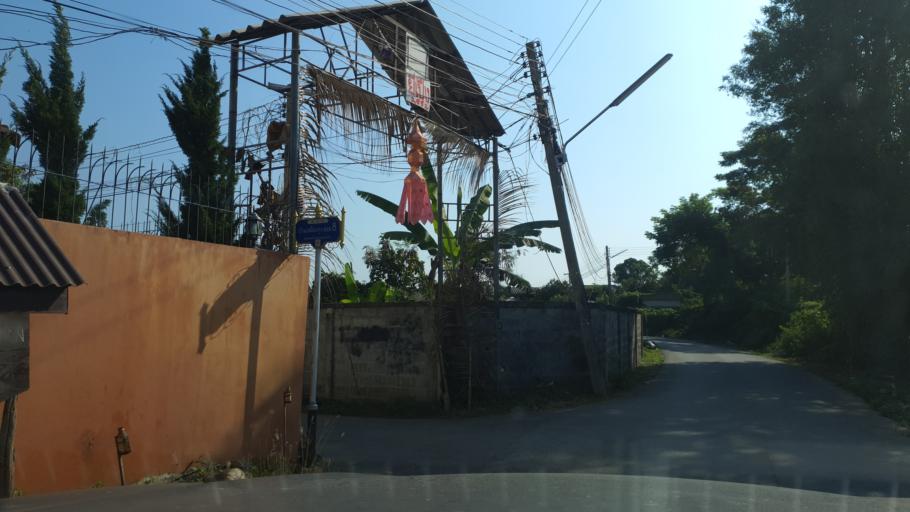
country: TH
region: Chiang Mai
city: Hang Dong
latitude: 18.7257
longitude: 98.9405
